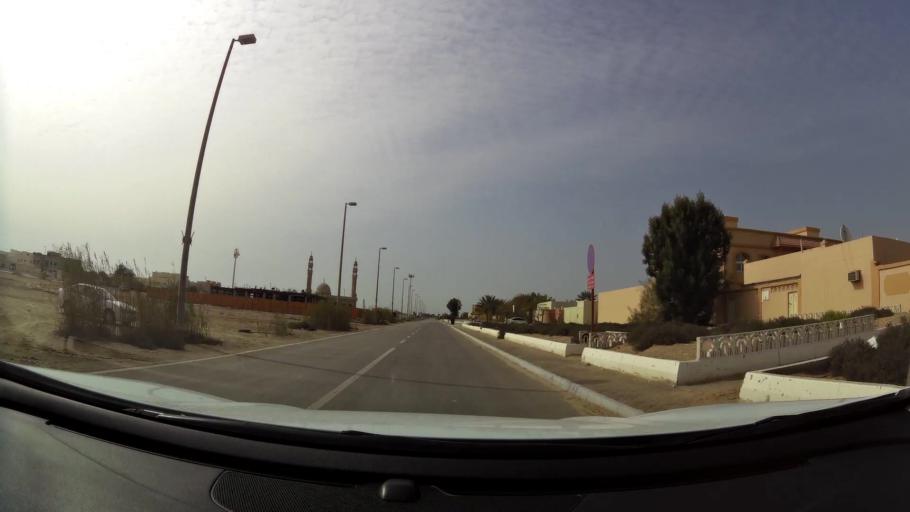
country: AE
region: Abu Dhabi
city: Abu Dhabi
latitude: 24.5917
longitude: 54.6973
